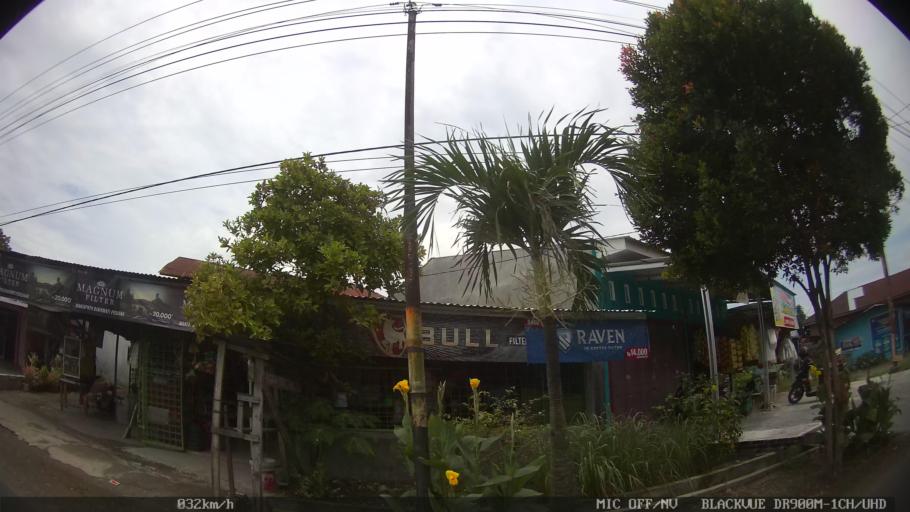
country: ID
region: North Sumatra
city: Binjai
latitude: 3.6256
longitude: 98.5558
